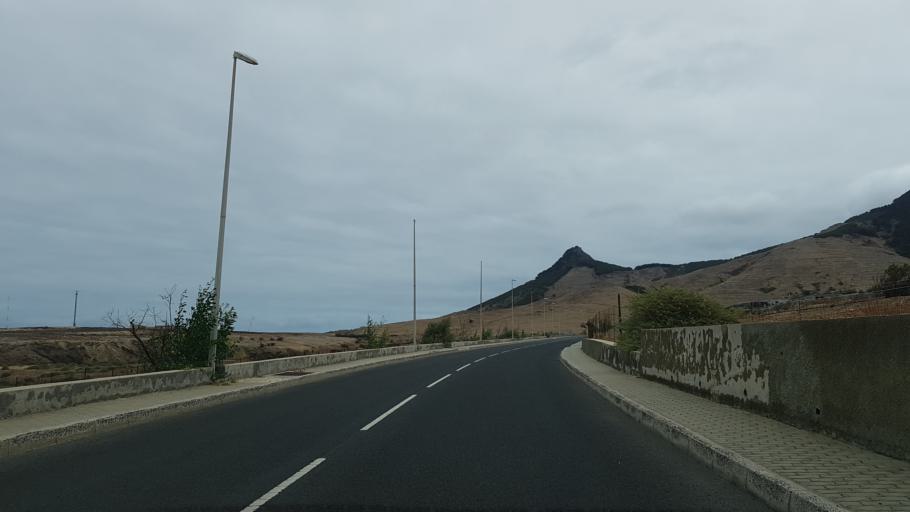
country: PT
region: Madeira
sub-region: Porto Santo
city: Camacha
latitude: 33.0896
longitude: -16.3445
